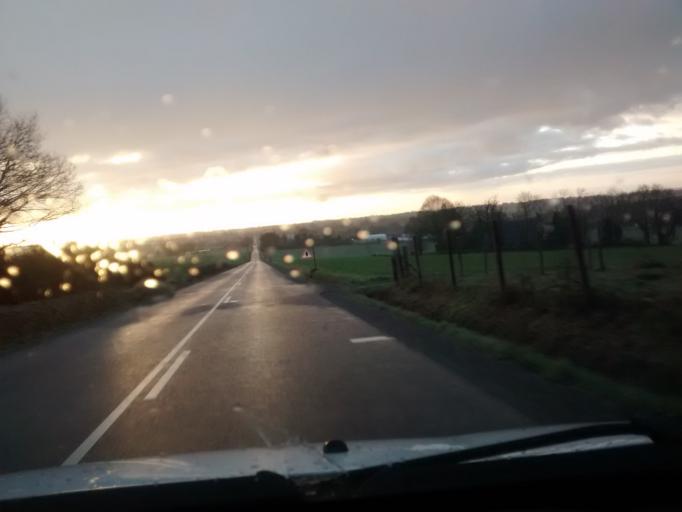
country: FR
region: Brittany
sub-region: Departement d'Ille-et-Vilaine
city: Bais
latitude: 48.0253
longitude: -1.3113
